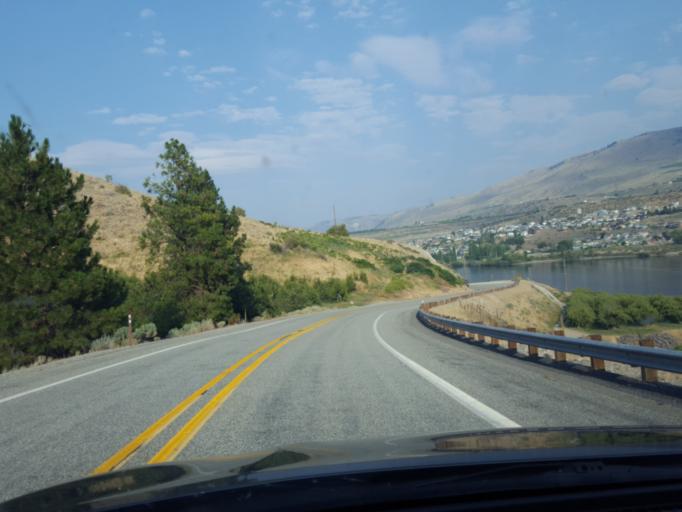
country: US
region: Washington
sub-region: Chelan County
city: Entiat
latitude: 47.7675
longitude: -120.1825
